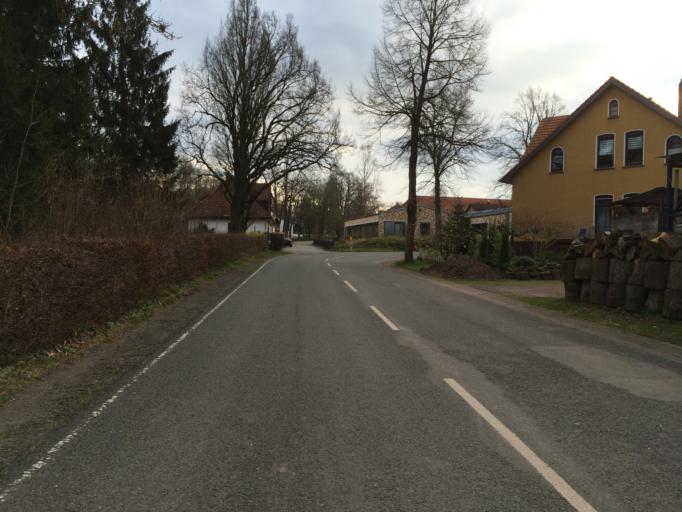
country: DE
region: North Rhine-Westphalia
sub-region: Regierungsbezirk Detmold
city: Schieder-Schwalenberg
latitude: 51.9174
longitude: 9.1491
